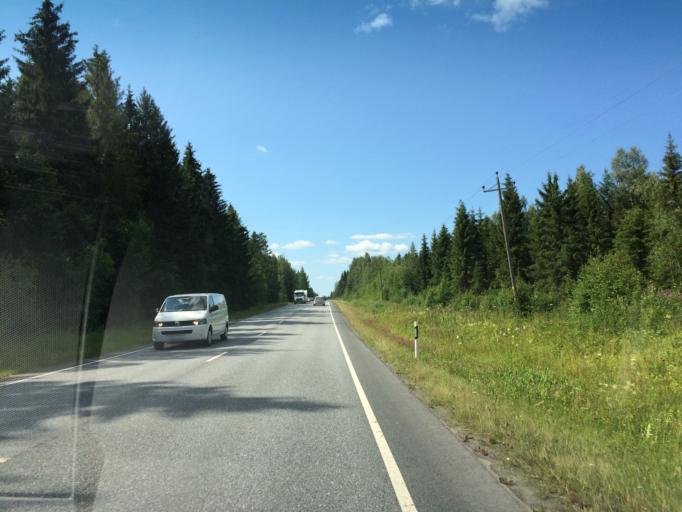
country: FI
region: Pirkanmaa
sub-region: Lounais-Pirkanmaa
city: Kiikoinen
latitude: 61.4849
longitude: 22.6488
